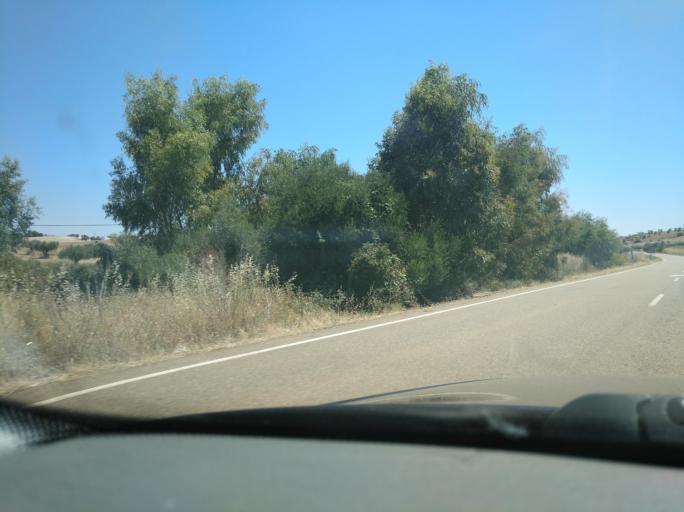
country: ES
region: Extremadura
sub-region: Provincia de Badajoz
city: Olivenza
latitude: 38.6986
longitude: -7.1450
